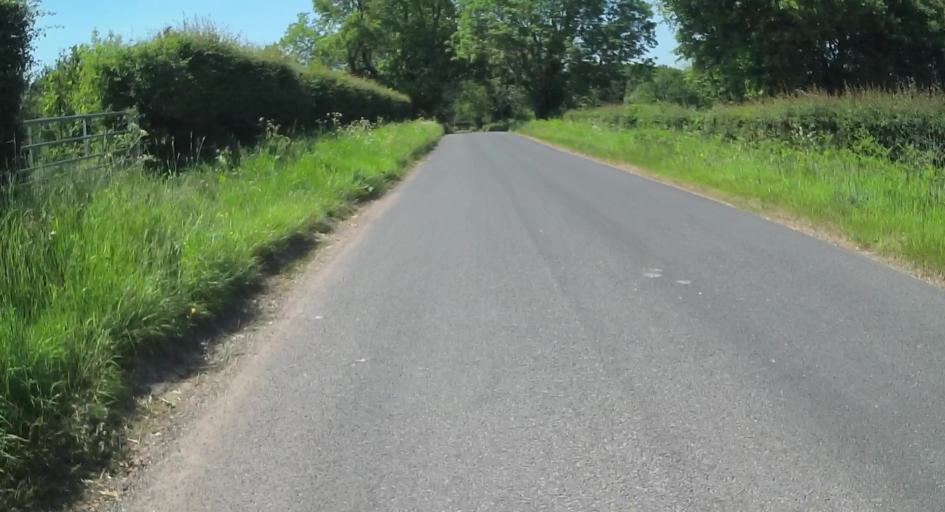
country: GB
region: England
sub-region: Hampshire
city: Kingsclere
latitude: 51.3458
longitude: -1.2044
